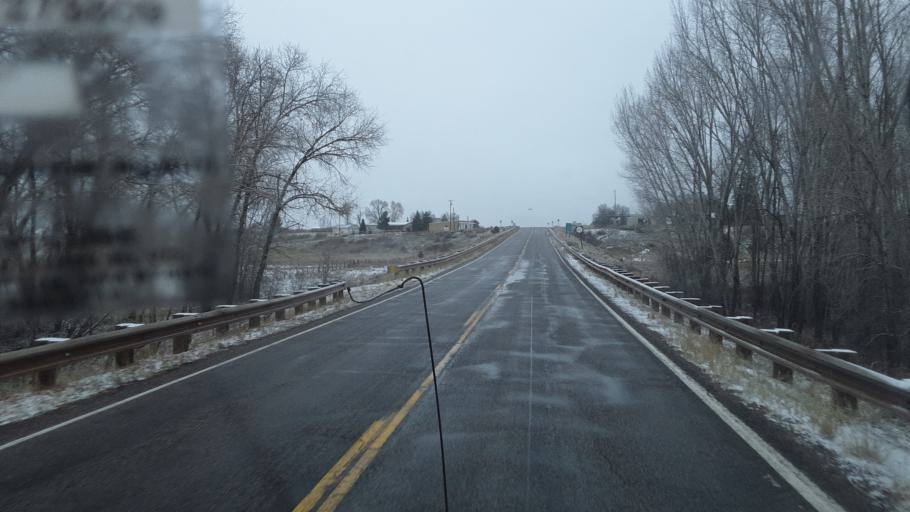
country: US
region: New Mexico
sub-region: Rio Arriba County
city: Tierra Amarilla
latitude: 36.6989
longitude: -106.5581
